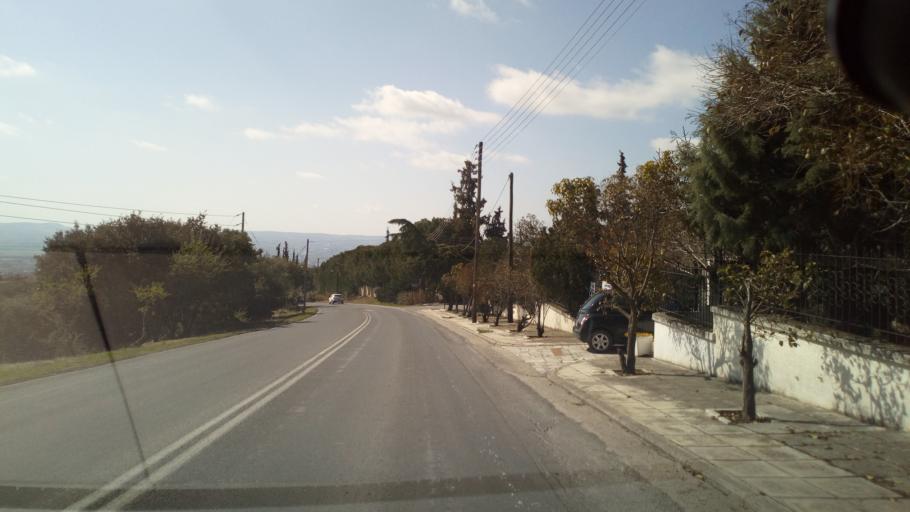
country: GR
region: Central Macedonia
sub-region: Nomos Thessalonikis
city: Panorama
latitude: 40.5742
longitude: 23.0253
